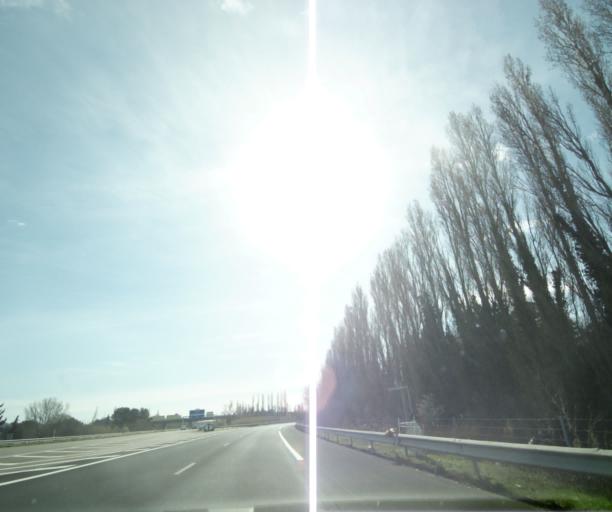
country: FR
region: Provence-Alpes-Cote d'Azur
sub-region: Departement du Vaucluse
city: Orange
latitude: 44.1322
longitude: 4.7875
